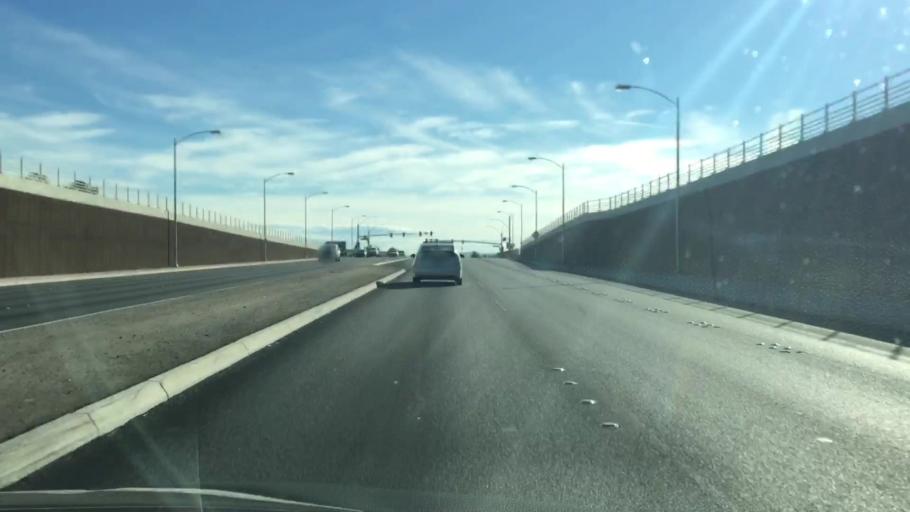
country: US
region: Nevada
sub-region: Clark County
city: Enterprise
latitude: 36.0594
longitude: -115.2079
